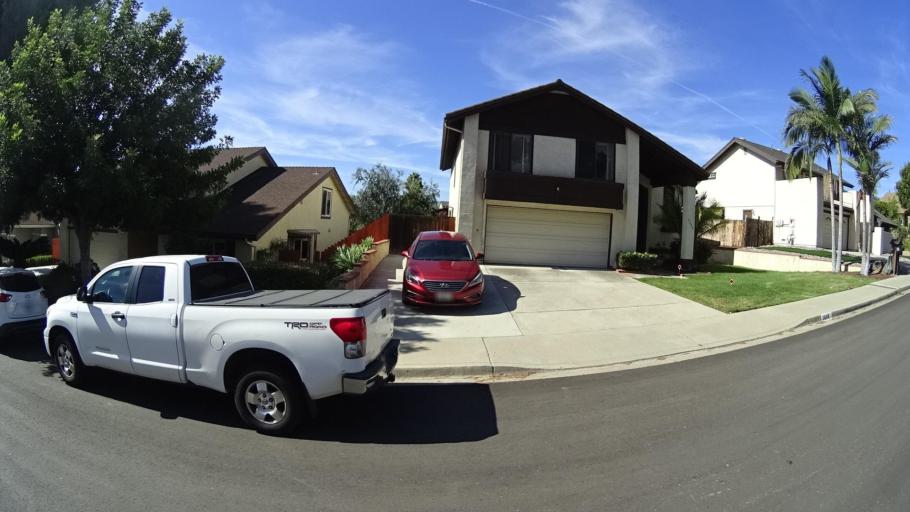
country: US
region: California
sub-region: San Diego County
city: Rancho San Diego
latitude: 32.7477
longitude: -116.9541
